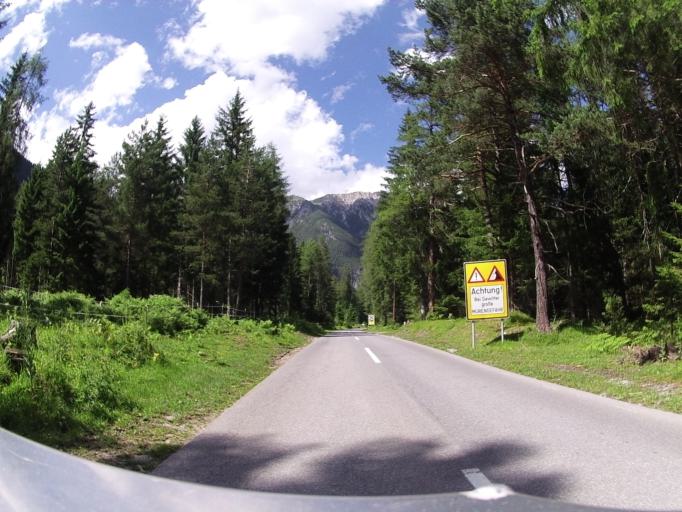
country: AT
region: Tyrol
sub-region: Politischer Bezirk Imst
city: Imst
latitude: 47.2688
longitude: 10.7421
